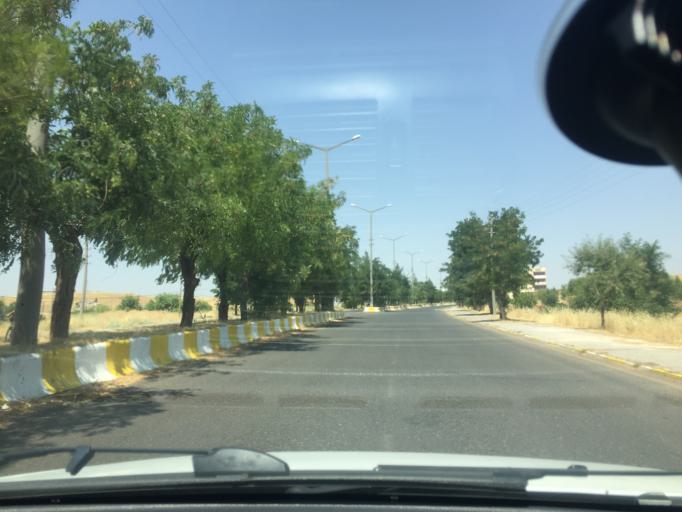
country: TR
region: Mardin
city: Kindirip
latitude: 37.4561
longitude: 41.2238
